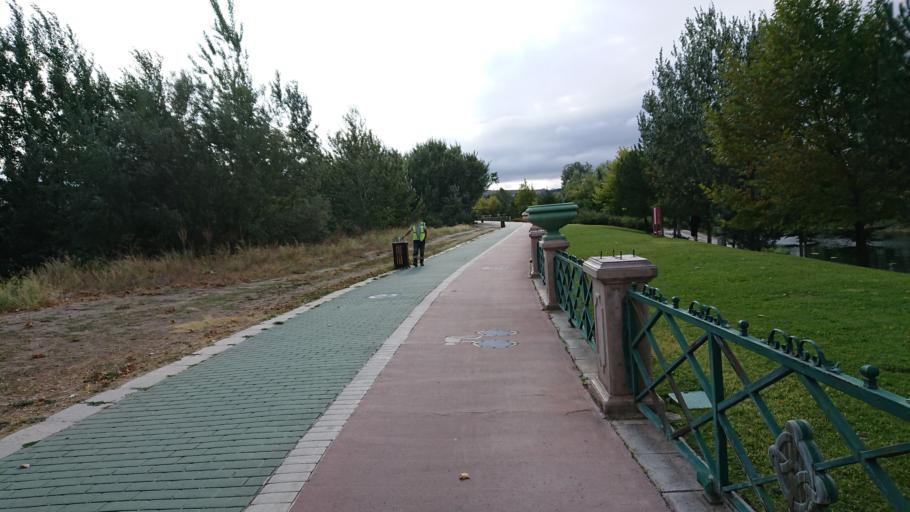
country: TR
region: Eskisehir
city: Eskisehir
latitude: 39.7601
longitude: 30.4845
